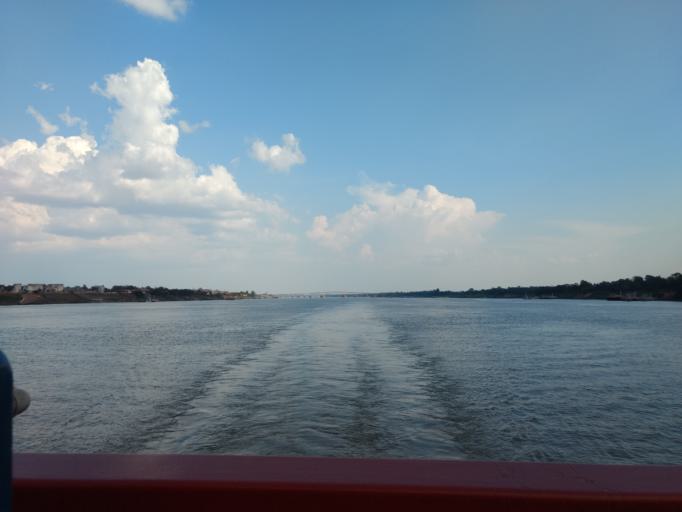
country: BR
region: Rondonia
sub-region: Porto Velho
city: Porto Velho
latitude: -8.7015
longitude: -63.9227
